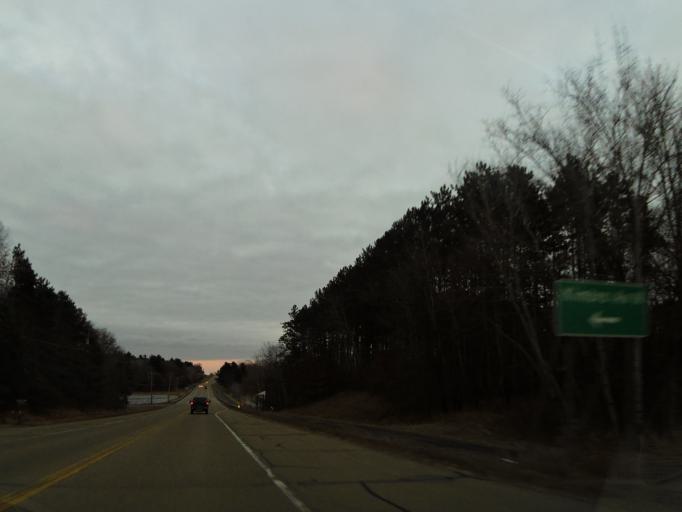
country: US
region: Minnesota
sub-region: Washington County
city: Grant
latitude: 45.0578
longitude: -92.8960
